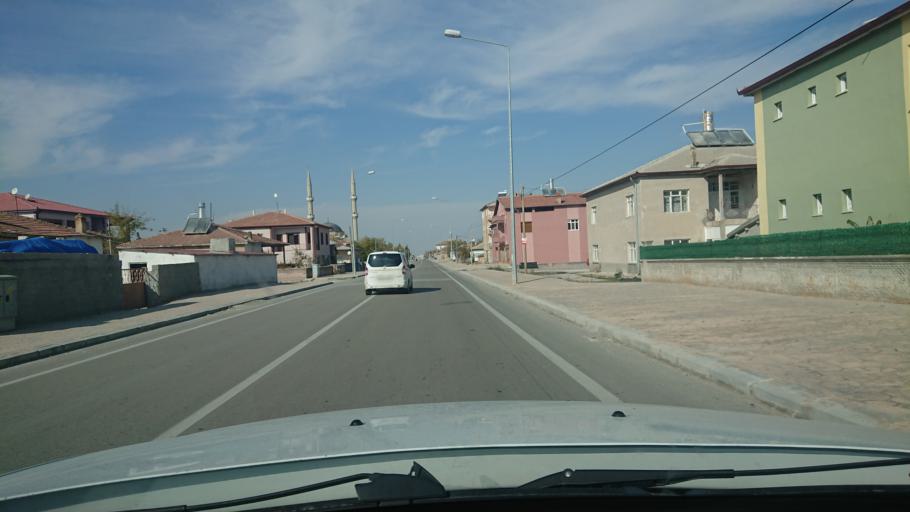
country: TR
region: Aksaray
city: Sultanhani
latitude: 38.2567
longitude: 33.4467
